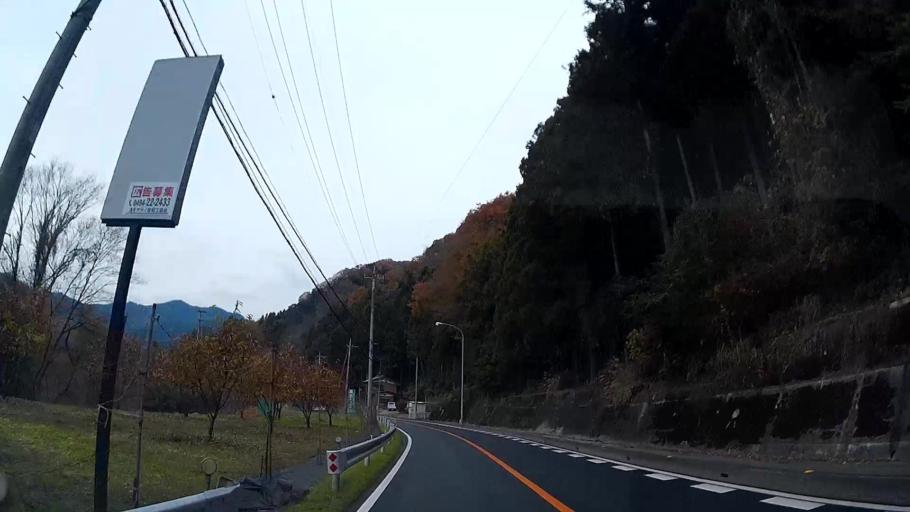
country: JP
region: Saitama
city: Chichibu
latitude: 35.9617
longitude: 139.0009
